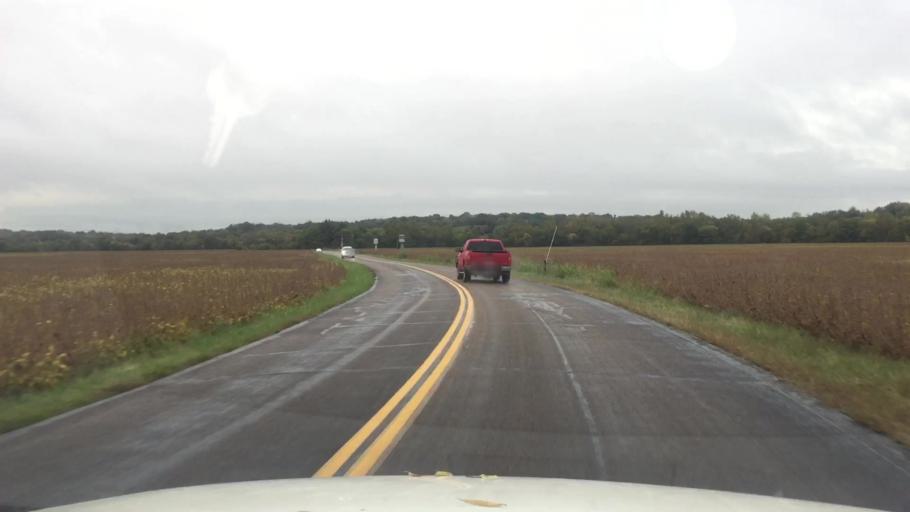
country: US
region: Missouri
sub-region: Boone County
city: Columbia
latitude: 38.8925
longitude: -92.4648
